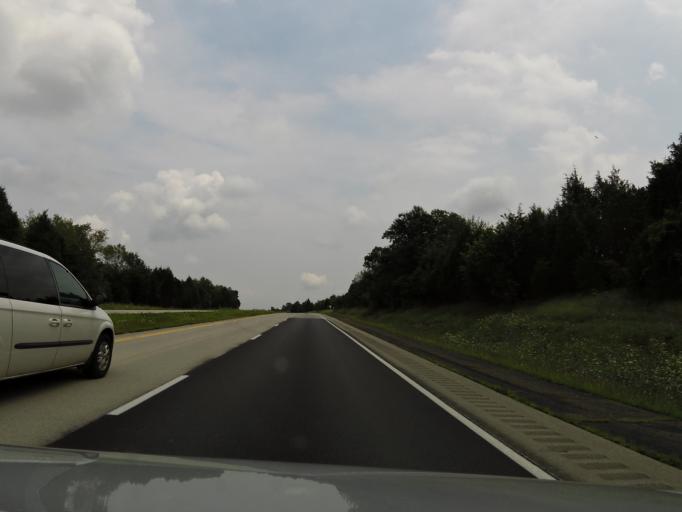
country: US
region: Kentucky
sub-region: Hardin County
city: Elizabethtown
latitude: 37.5632
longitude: -86.0586
